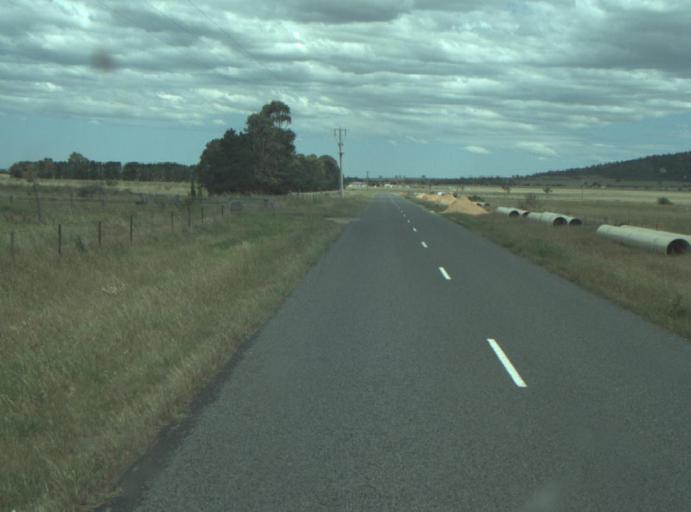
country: AU
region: Victoria
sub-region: Wyndham
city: Little River
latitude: -37.9082
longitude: 144.4632
